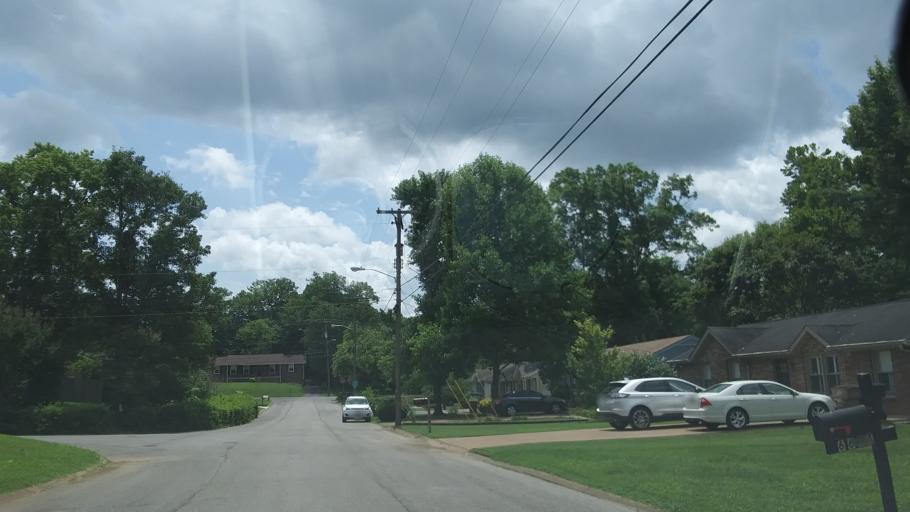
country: US
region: Tennessee
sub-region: Davidson County
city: Belle Meade
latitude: 36.1383
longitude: -86.8937
